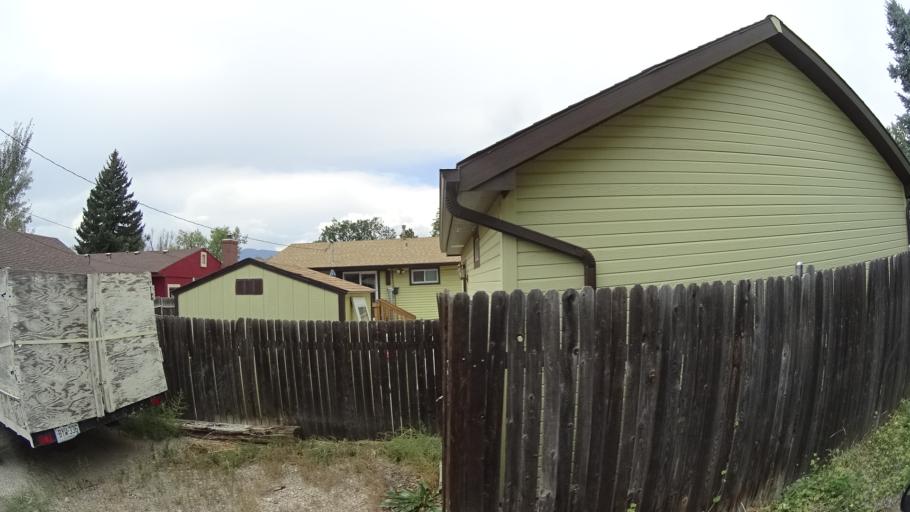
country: US
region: Colorado
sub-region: El Paso County
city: Colorado Springs
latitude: 38.8683
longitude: -104.7885
